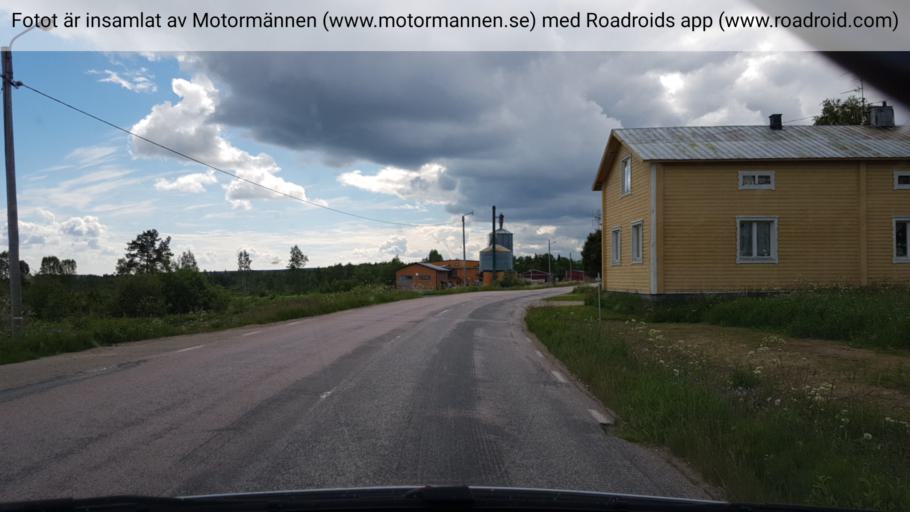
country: FI
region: Lapland
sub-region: Torniolaakso
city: Ylitornio
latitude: 66.2246
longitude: 23.6921
